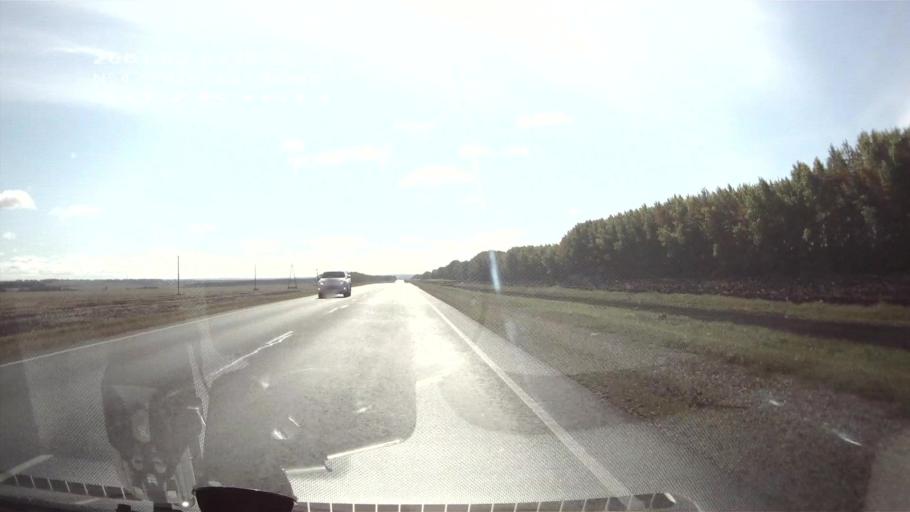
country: RU
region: Ulyanovsk
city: Tsil'na
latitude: 54.5706
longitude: 47.9107
